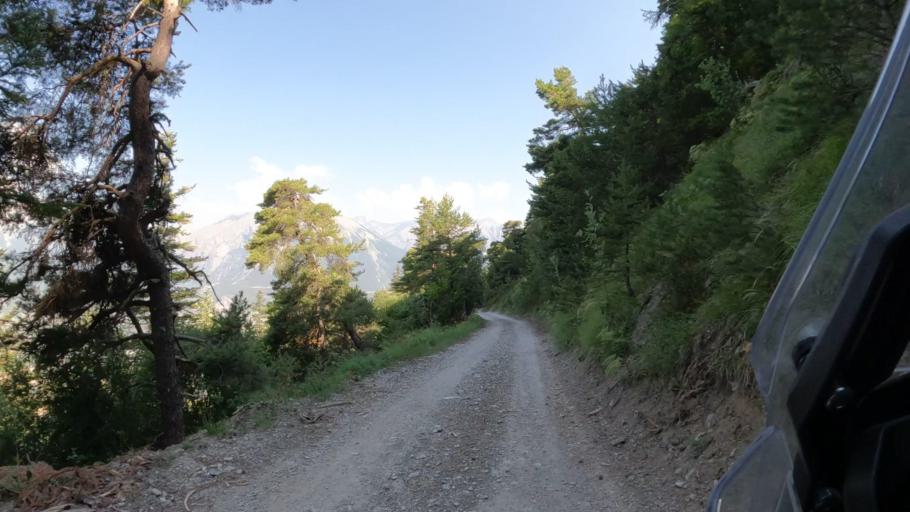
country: FR
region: Provence-Alpes-Cote d'Azur
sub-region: Departement des Hautes-Alpes
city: Embrun
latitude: 44.5957
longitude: 6.5649
